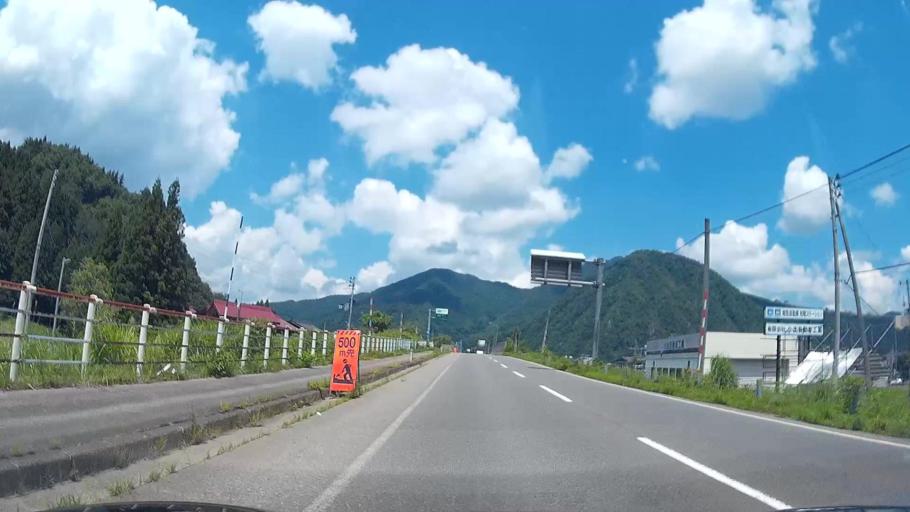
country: JP
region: Niigata
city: Shiozawa
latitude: 36.9262
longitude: 138.8240
